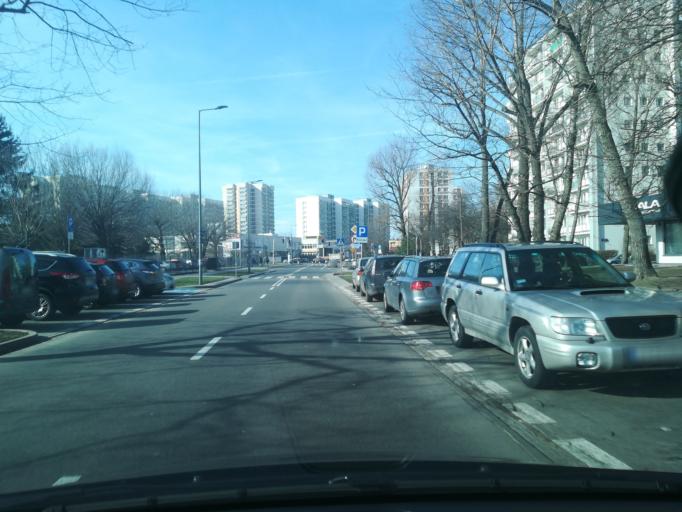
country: PL
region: Masovian Voivodeship
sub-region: Warszawa
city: Praga Poludnie
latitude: 52.2410
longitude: 21.0727
